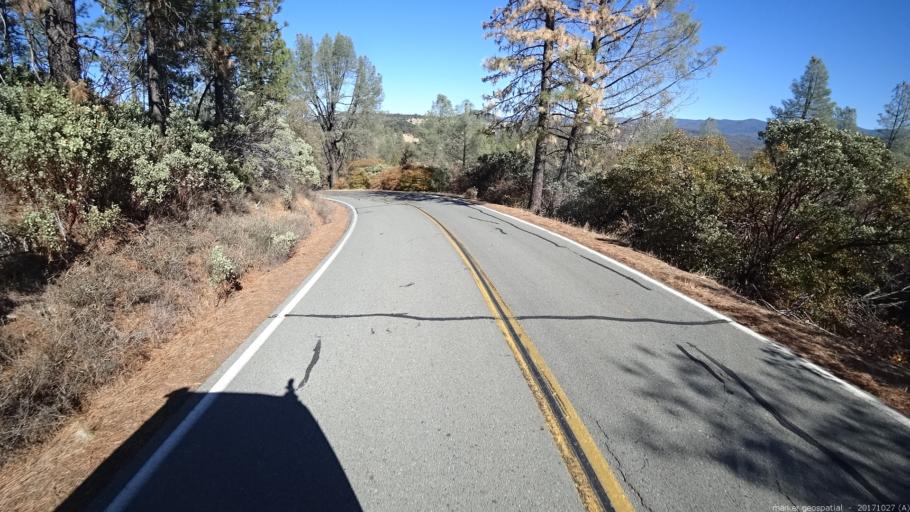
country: US
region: California
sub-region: Shasta County
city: Bella Vista
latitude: 40.7301
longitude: -122.0141
